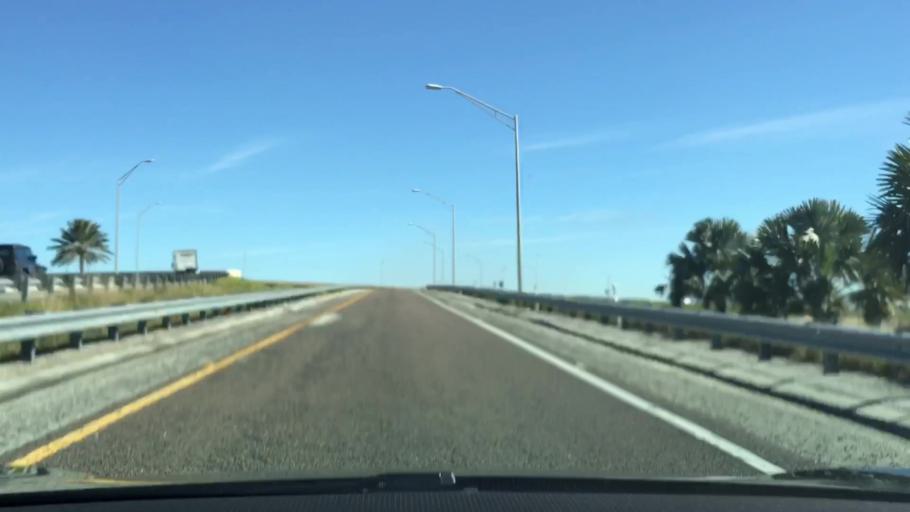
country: US
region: Florida
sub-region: Orange County
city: Ocoee
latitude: 28.5458
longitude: -81.5619
